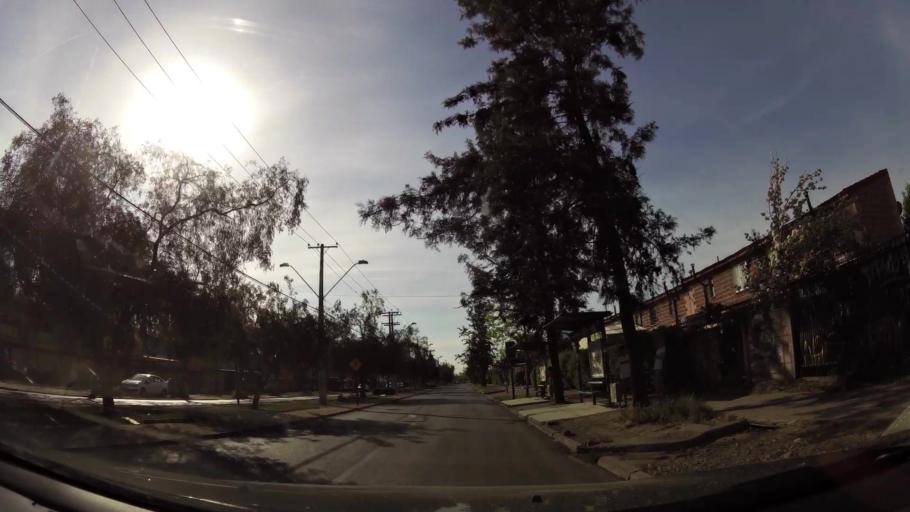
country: CL
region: Santiago Metropolitan
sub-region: Provincia de Cordillera
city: Puente Alto
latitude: -33.5905
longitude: -70.5614
